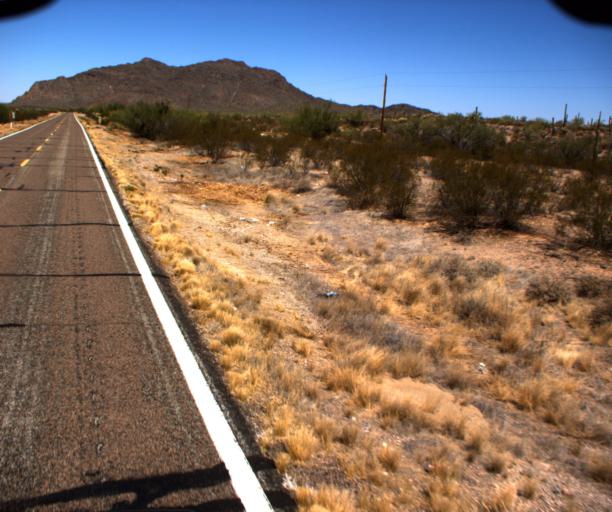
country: US
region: Arizona
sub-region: Pima County
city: Ajo
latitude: 32.2206
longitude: -112.6627
